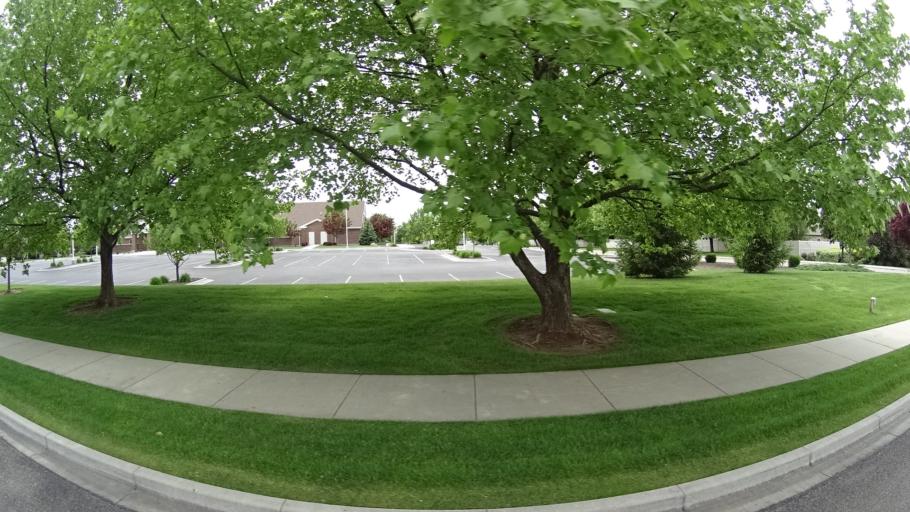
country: US
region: Idaho
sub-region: Ada County
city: Meridian
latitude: 43.6464
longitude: -116.4150
